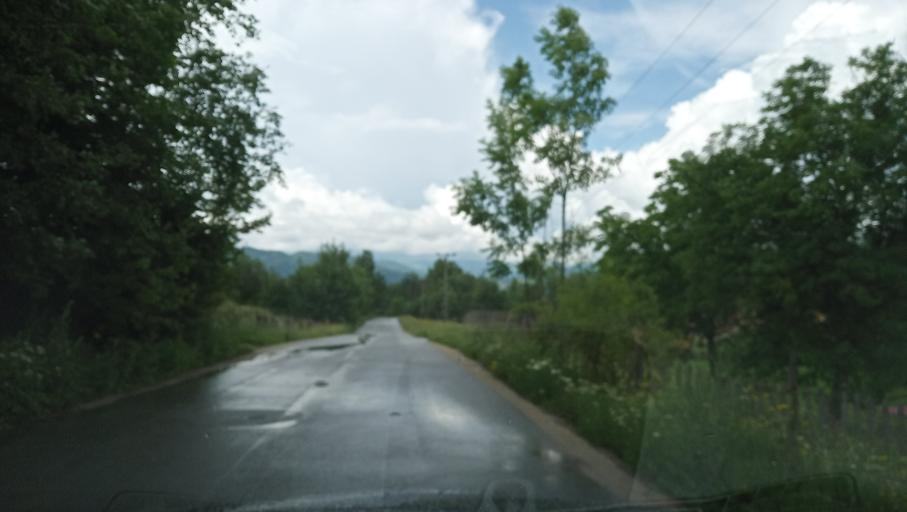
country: RO
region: Hunedoara
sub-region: Oras Petrila
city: Petrila
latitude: 45.4133
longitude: 23.4119
